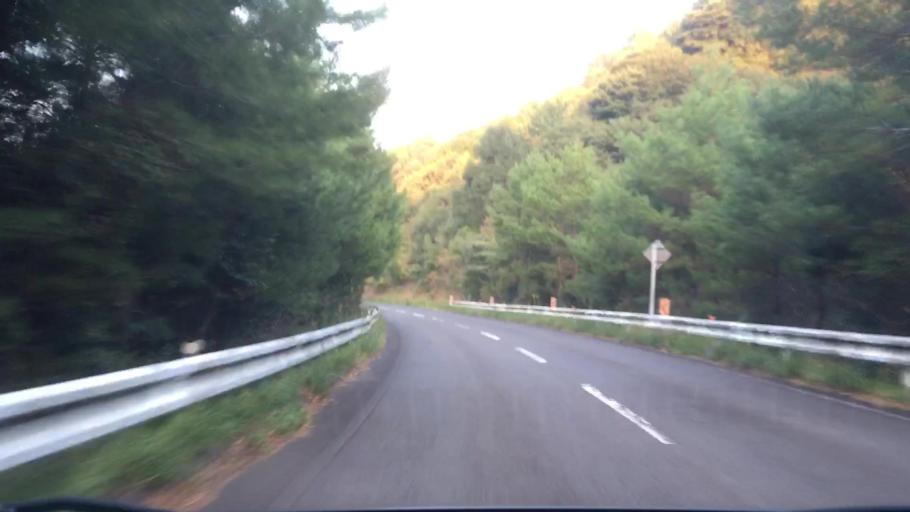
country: JP
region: Nagasaki
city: Sasebo
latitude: 32.9952
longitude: 129.7159
